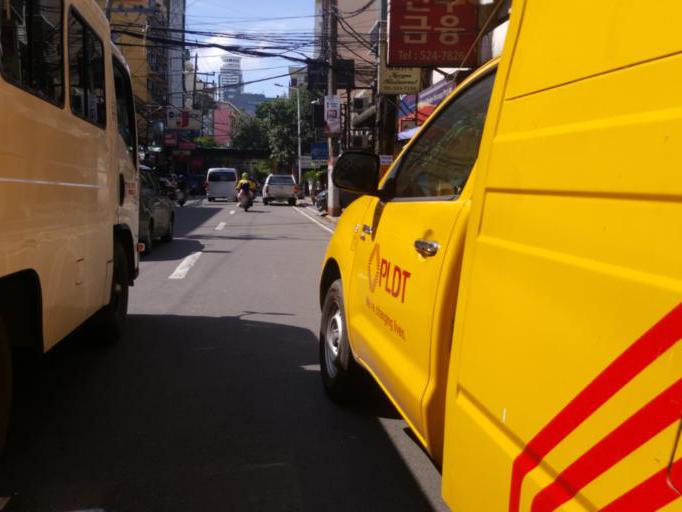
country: PH
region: Metro Manila
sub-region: City of Manila
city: Port Area
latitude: 14.5742
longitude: 120.9829
